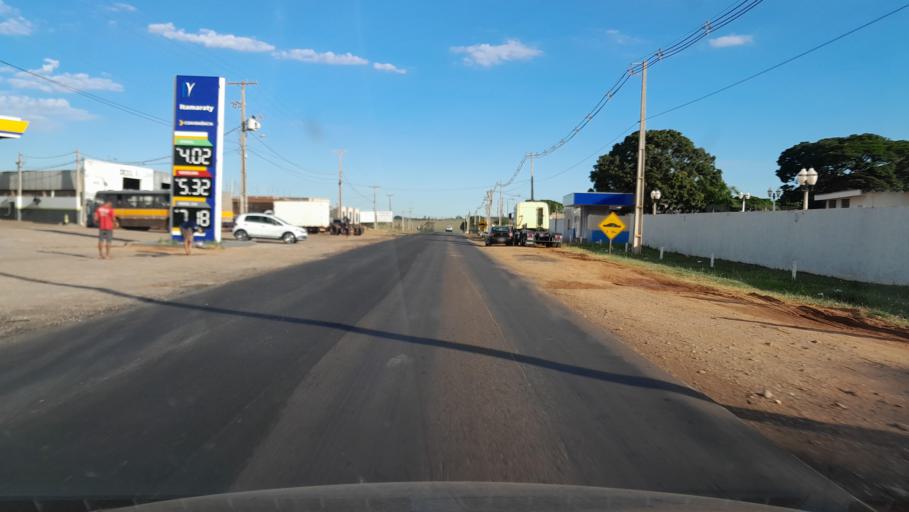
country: BR
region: Parana
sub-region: Umuarama
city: Umuarama
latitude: -23.7720
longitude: -53.2689
